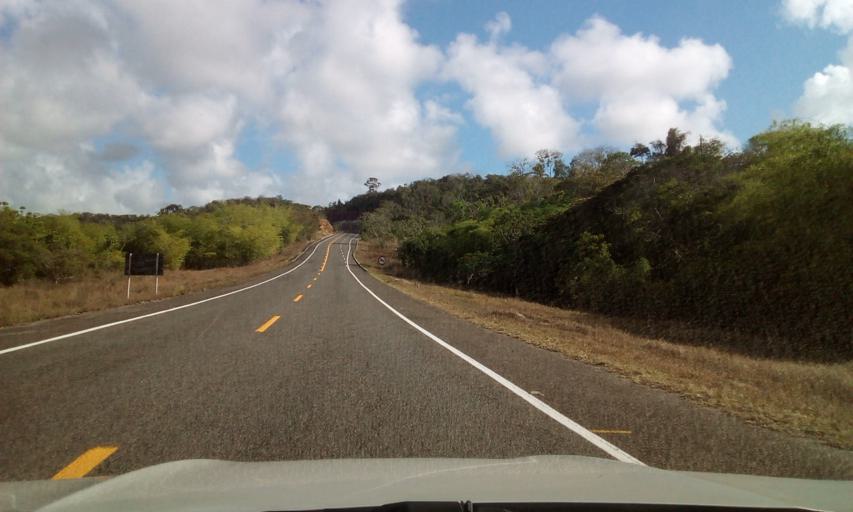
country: BR
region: Bahia
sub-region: Conde
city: Conde
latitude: -11.7694
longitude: -37.5913
